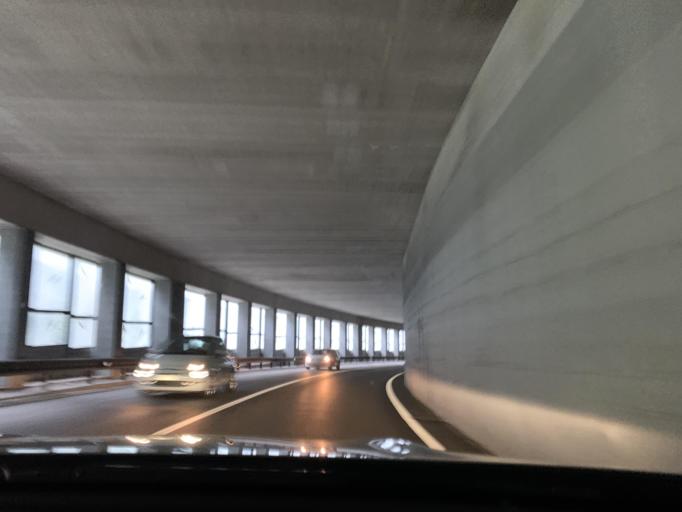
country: IT
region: Trentino-Alto Adige
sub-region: Bolzano
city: Nova Ponente
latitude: 46.4537
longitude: 11.4374
